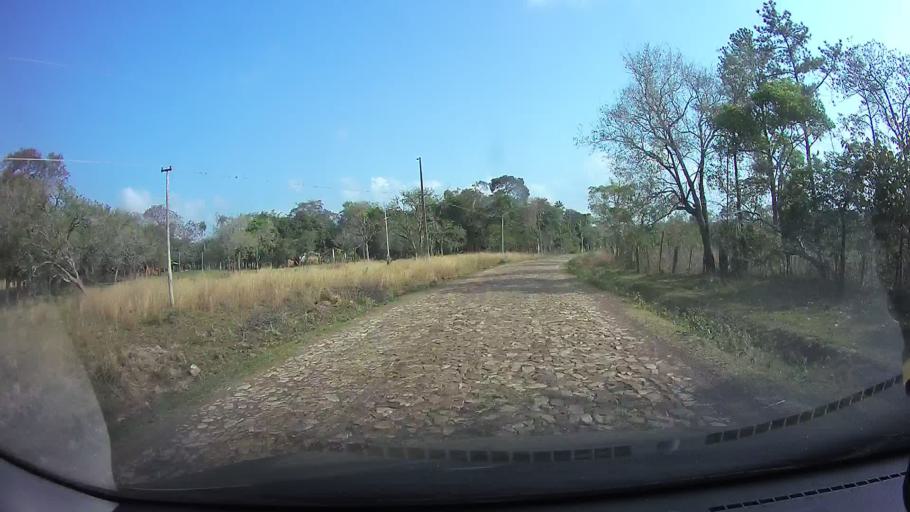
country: PY
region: Cordillera
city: Arroyos y Esteros
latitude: -25.0012
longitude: -57.1958
